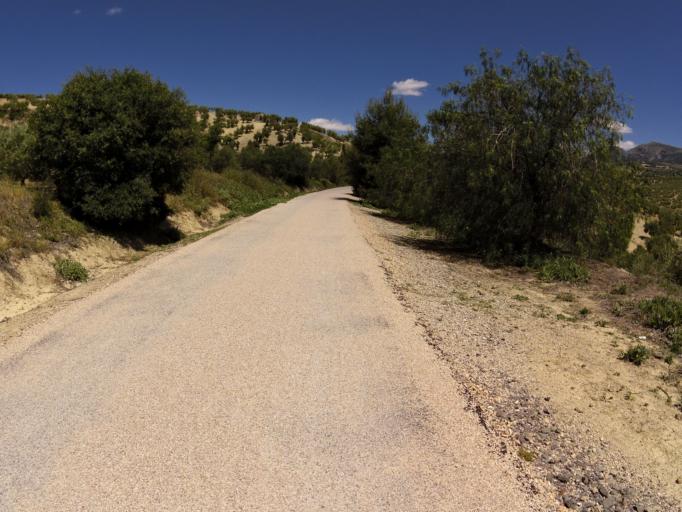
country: ES
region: Andalusia
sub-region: Provincia de Jaen
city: Torre del Campo
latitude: 37.7717
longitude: -3.9166
